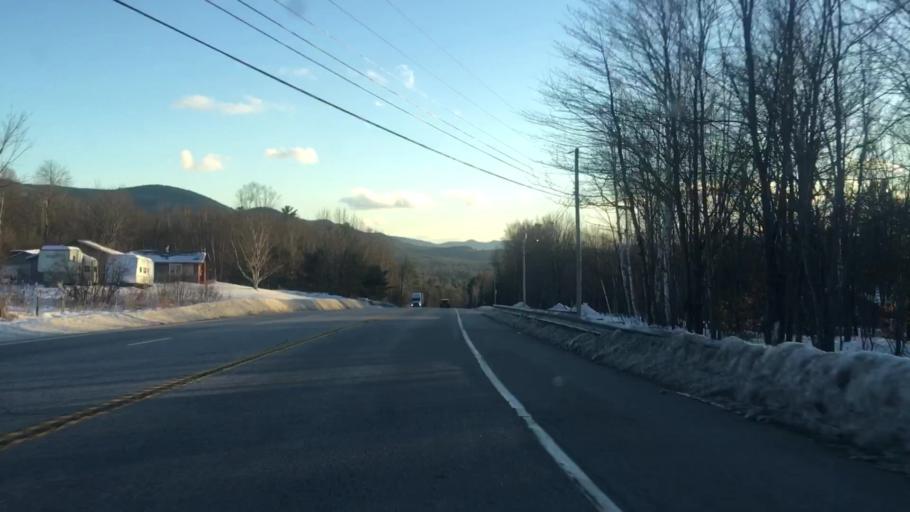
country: US
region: Maine
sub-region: Oxford County
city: Peru
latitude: 44.5822
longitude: -70.3695
